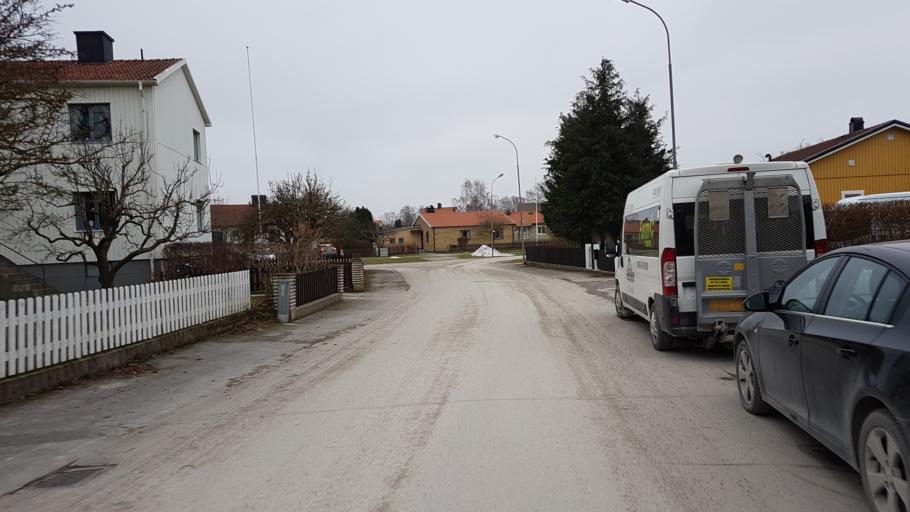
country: SE
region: Gotland
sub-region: Gotland
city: Visby
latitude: 57.6335
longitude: 18.3178
